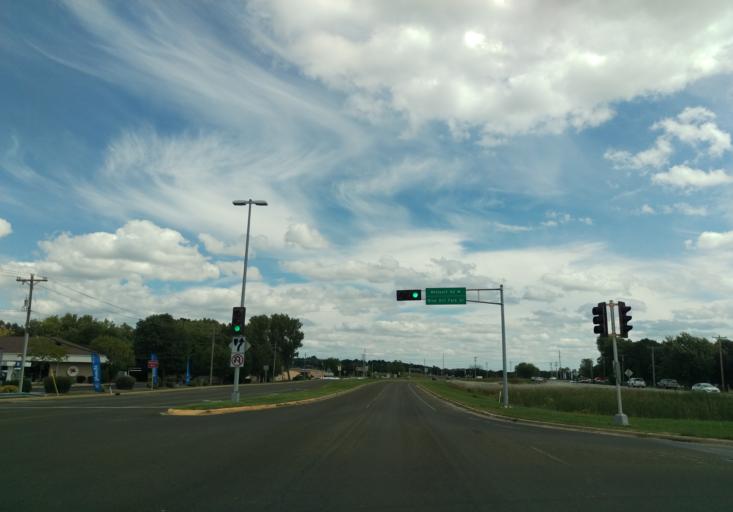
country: US
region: Wisconsin
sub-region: Dane County
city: Maple Bluff
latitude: 43.1523
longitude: -89.4105
